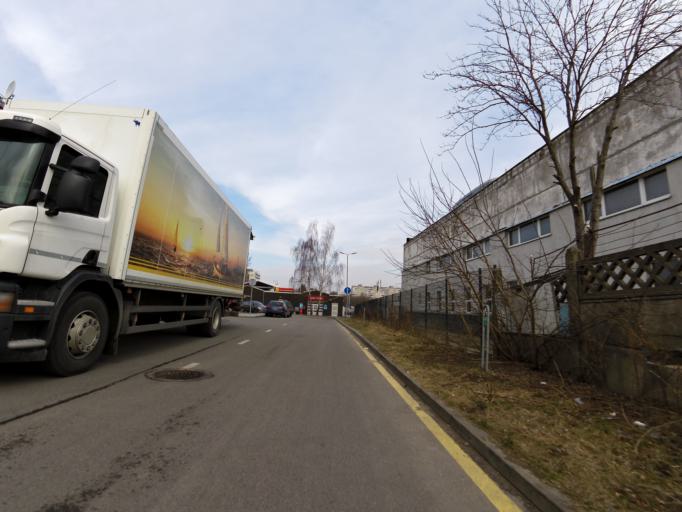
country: LT
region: Vilnius County
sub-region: Vilnius
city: Vilnius
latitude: 54.7179
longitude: 25.3007
